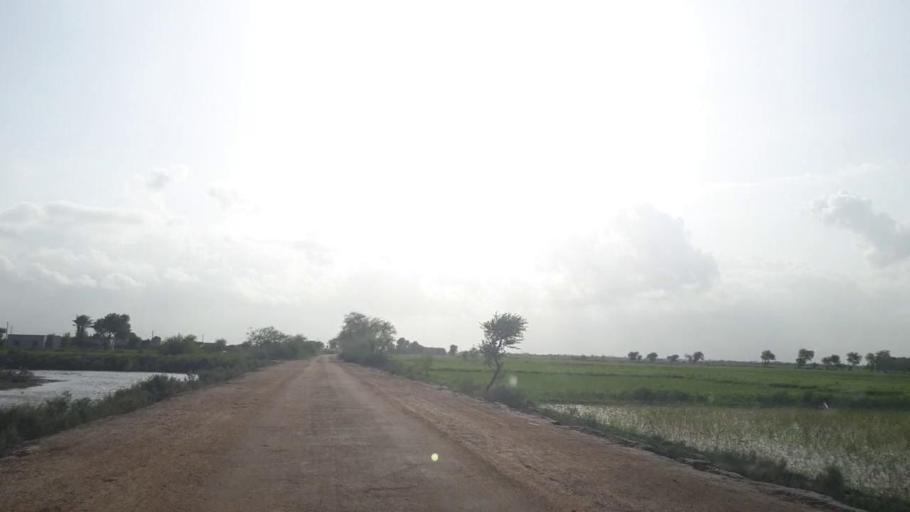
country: PK
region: Sindh
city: Kadhan
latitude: 24.6264
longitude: 69.0948
